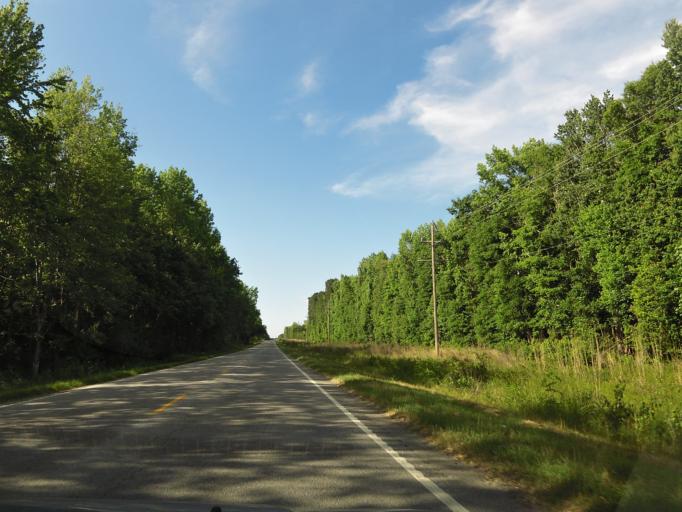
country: US
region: South Carolina
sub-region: Allendale County
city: Fairfax
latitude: 32.9150
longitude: -81.2375
